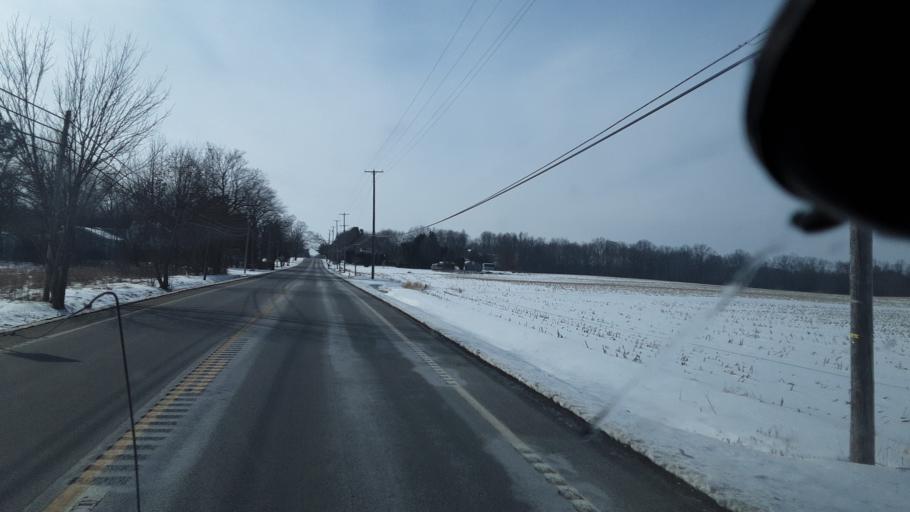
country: US
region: Ohio
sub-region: Stark County
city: Alliance
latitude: 41.0237
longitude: -81.1391
